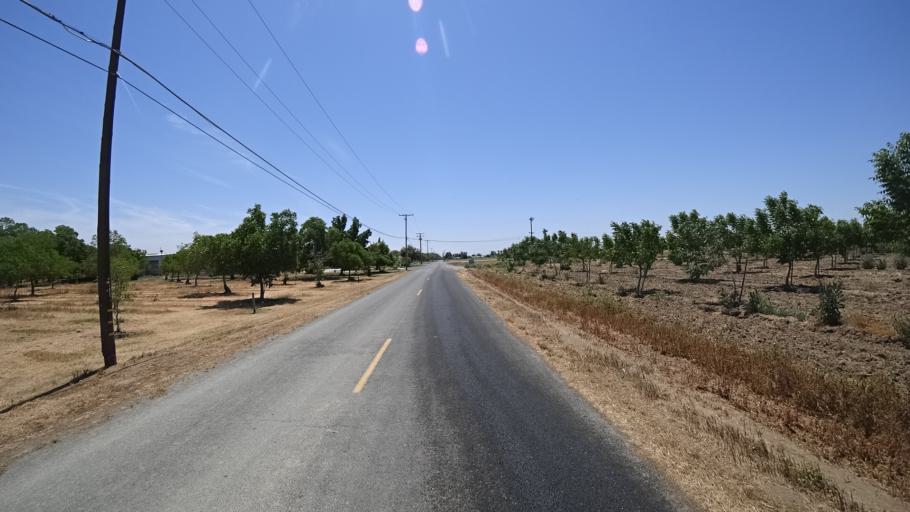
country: US
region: California
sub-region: Kings County
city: Armona
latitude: 36.3215
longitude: -119.7180
